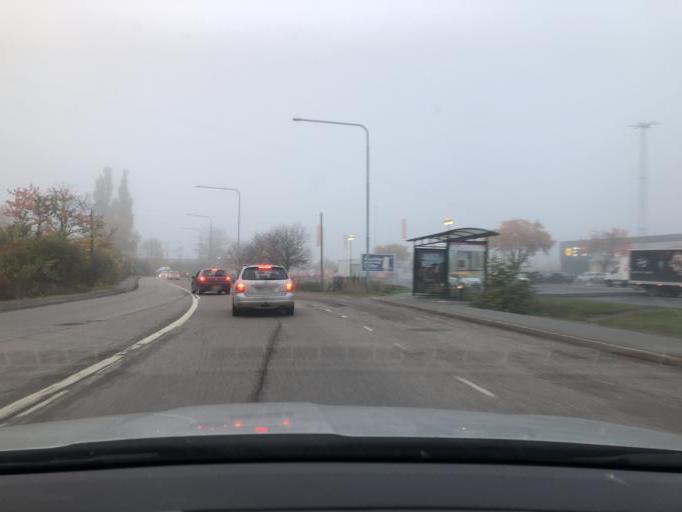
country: SE
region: Stockholm
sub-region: Botkyrka Kommun
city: Fittja
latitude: 59.2522
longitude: 17.8761
